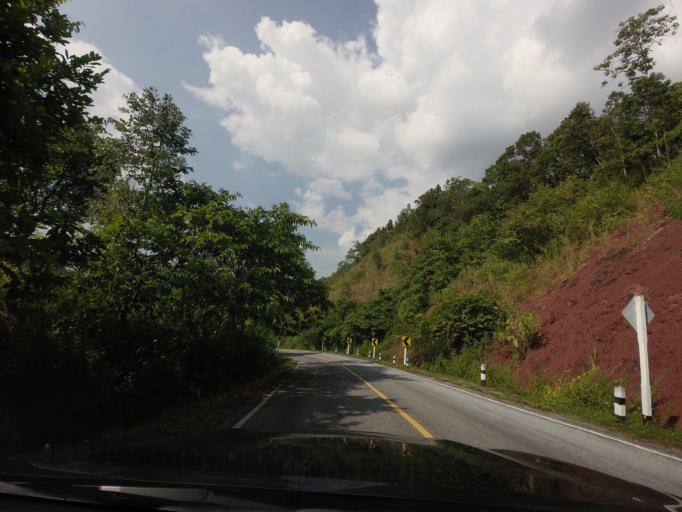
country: TH
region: Uttaradit
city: Ban Khok
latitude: 18.2566
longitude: 100.9934
